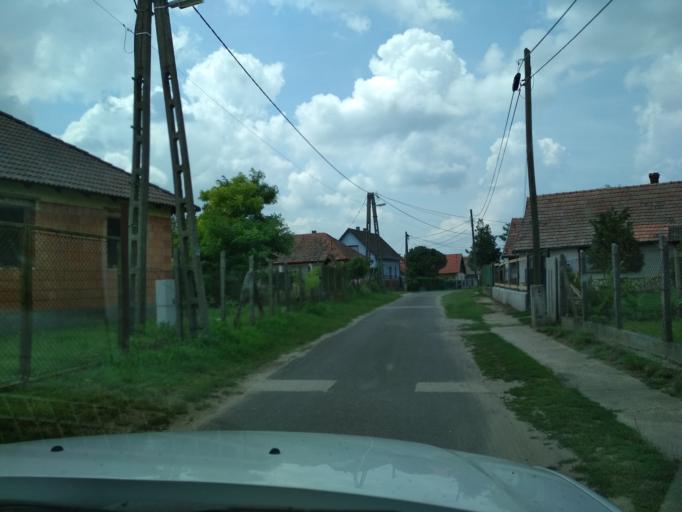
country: HU
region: Pest
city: Tapiobicske
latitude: 47.3615
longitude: 19.6783
